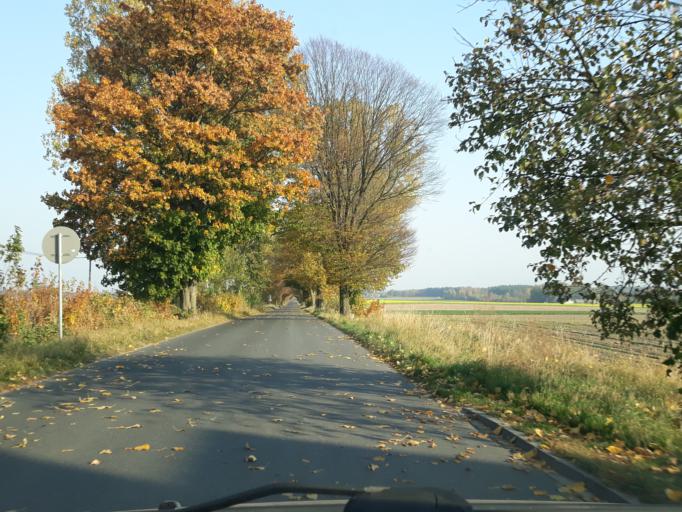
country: PL
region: Kujawsko-Pomorskie
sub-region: Powiat sepolenski
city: Sepolno Krajenskie
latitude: 53.4662
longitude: 17.4977
